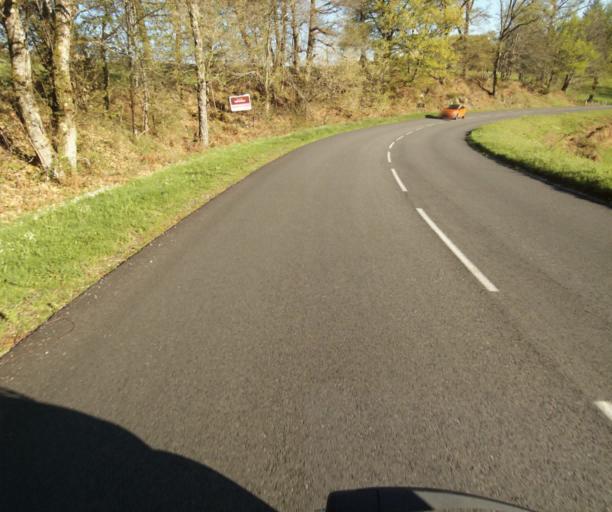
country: FR
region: Limousin
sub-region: Departement de la Correze
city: Correze
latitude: 45.3533
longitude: 1.8754
